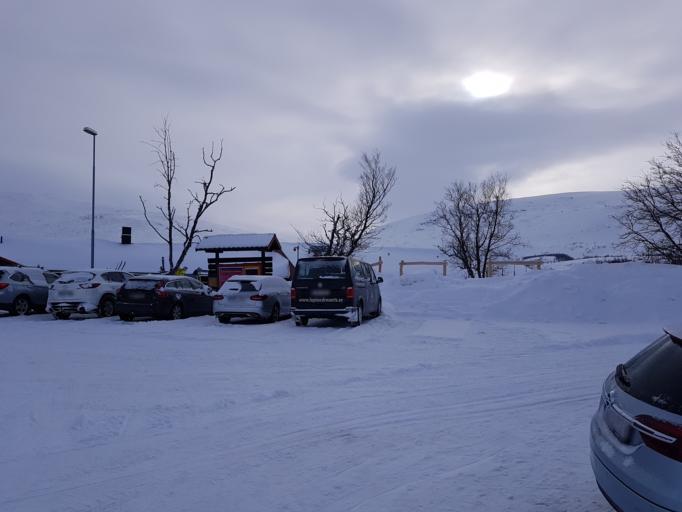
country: NO
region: Troms
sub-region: Bardu
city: Setermoen
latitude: 68.4070
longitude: 18.6749
